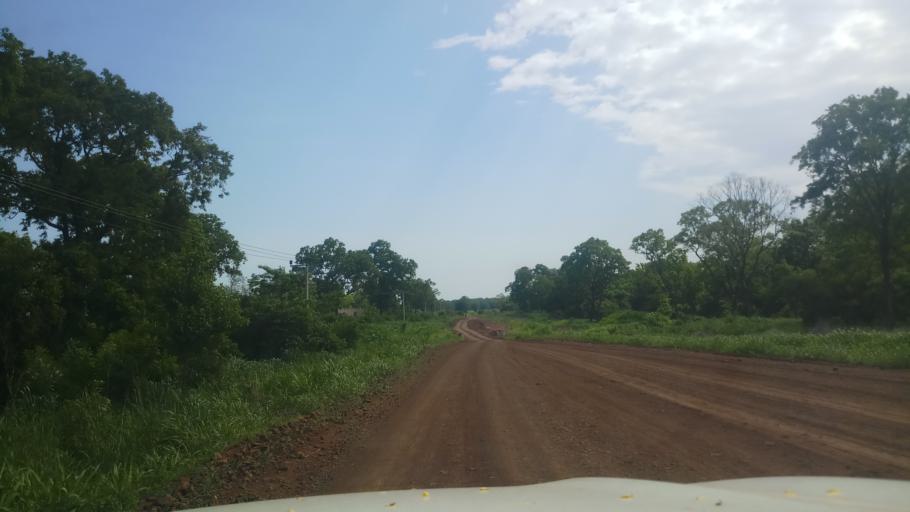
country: ET
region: Gambela
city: Gambela
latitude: 8.2071
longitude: 34.5144
